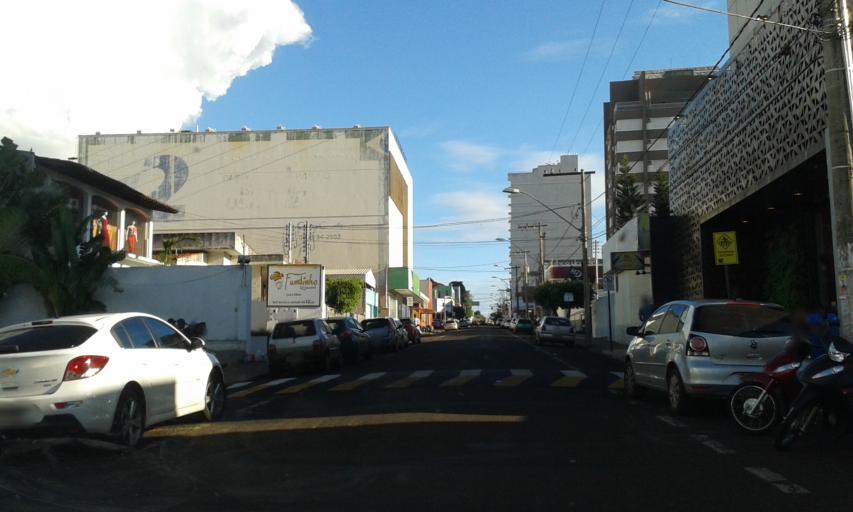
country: BR
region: Minas Gerais
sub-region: Ituiutaba
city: Ituiutaba
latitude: -18.9725
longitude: -49.4618
